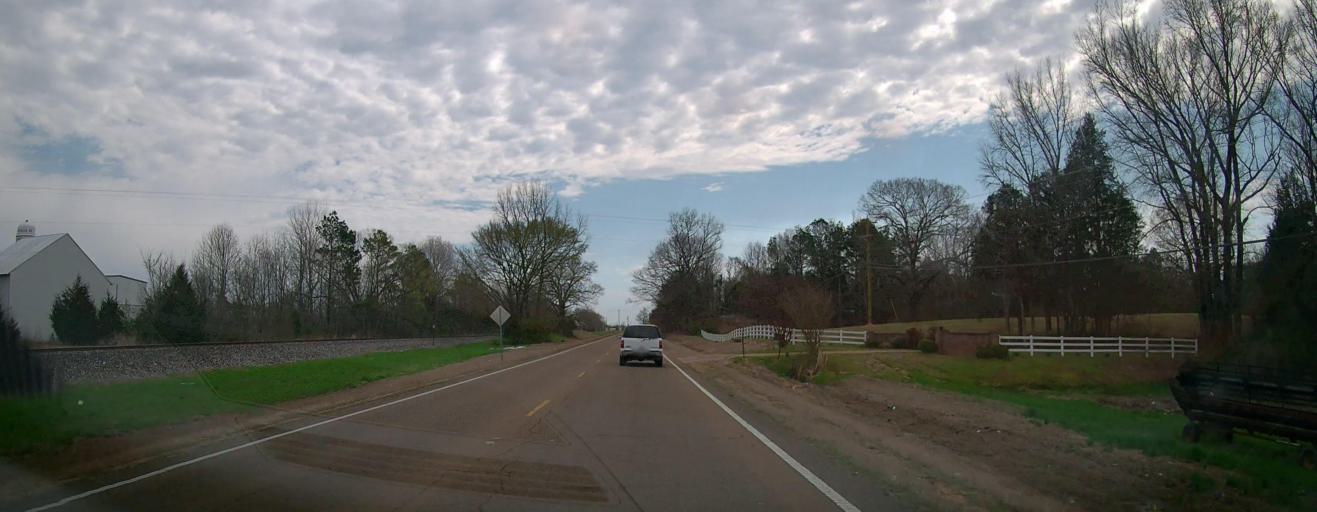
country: US
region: Mississippi
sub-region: Marshall County
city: Byhalia
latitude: 34.8699
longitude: -89.6745
